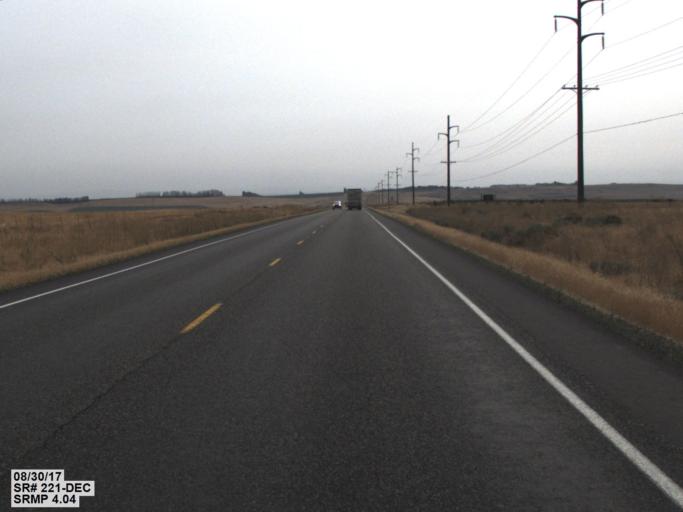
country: US
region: Oregon
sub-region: Morrow County
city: Irrigon
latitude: 45.9936
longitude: -119.6029
